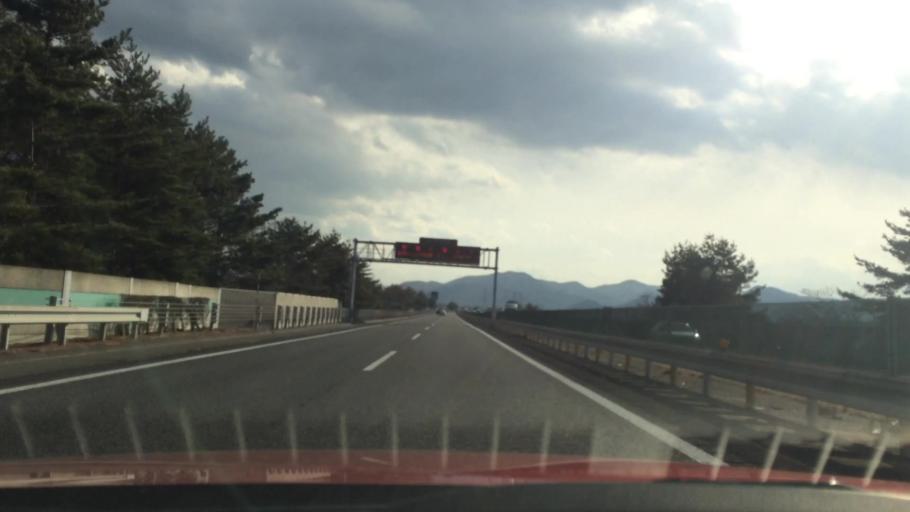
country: JP
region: Nagano
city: Shiojiri
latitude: 36.1560
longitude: 137.9680
